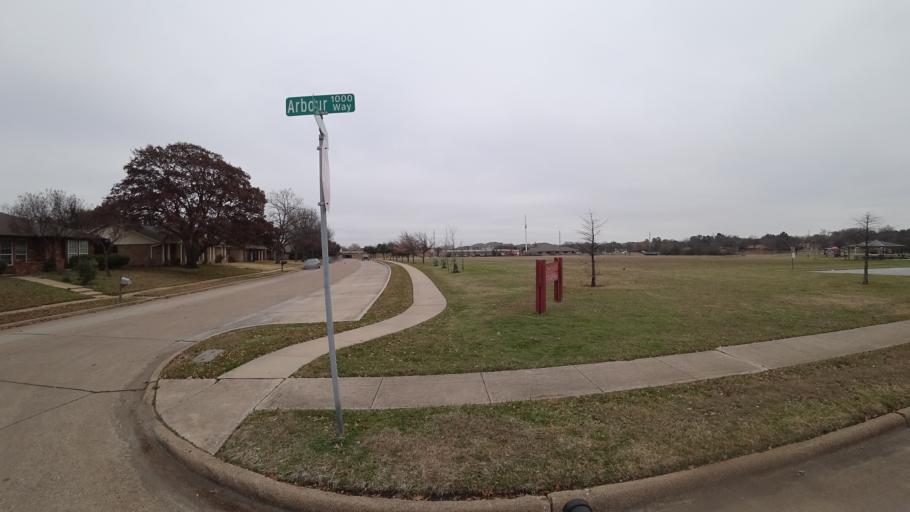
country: US
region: Texas
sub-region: Denton County
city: Highland Village
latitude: 33.0559
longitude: -97.0389
